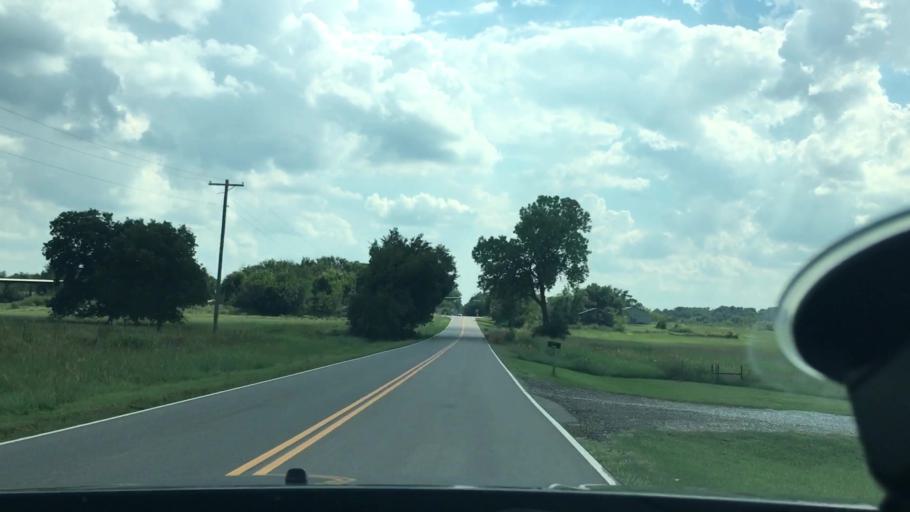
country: US
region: Oklahoma
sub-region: Pottawatomie County
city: Shawnee
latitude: 35.3364
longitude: -96.8072
